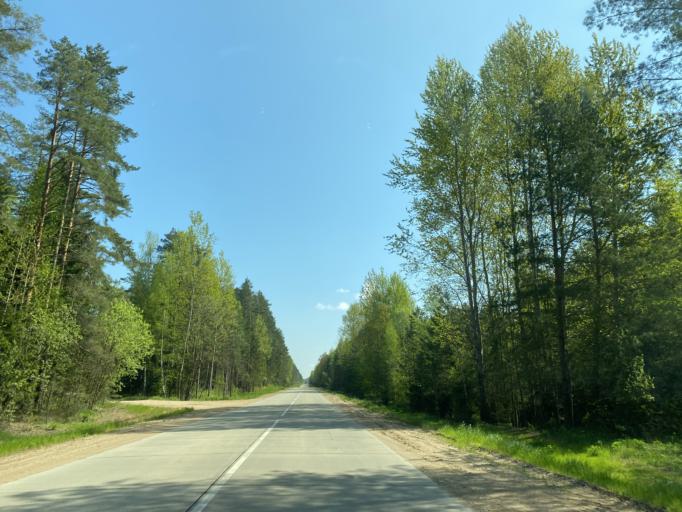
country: BY
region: Minsk
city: Horad Barysaw
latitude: 54.1677
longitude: 28.5099
